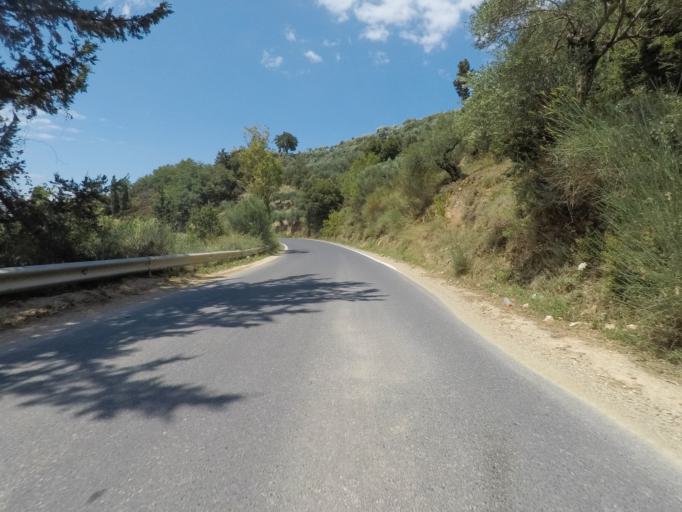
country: GR
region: Crete
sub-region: Nomos Irakleiou
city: Mokhos
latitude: 35.2264
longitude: 25.4622
